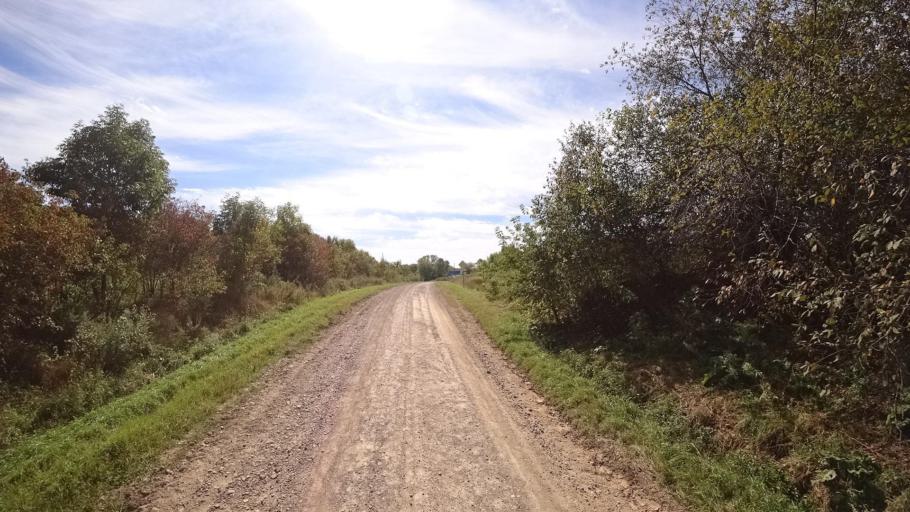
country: RU
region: Primorskiy
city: Kirovskiy
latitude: 44.7604
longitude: 133.6110
